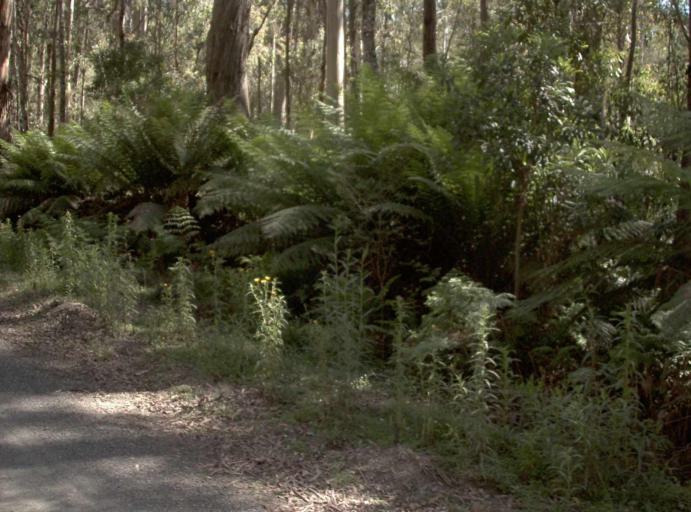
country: AU
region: New South Wales
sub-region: Bombala
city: Bombala
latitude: -37.2380
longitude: 148.7560
